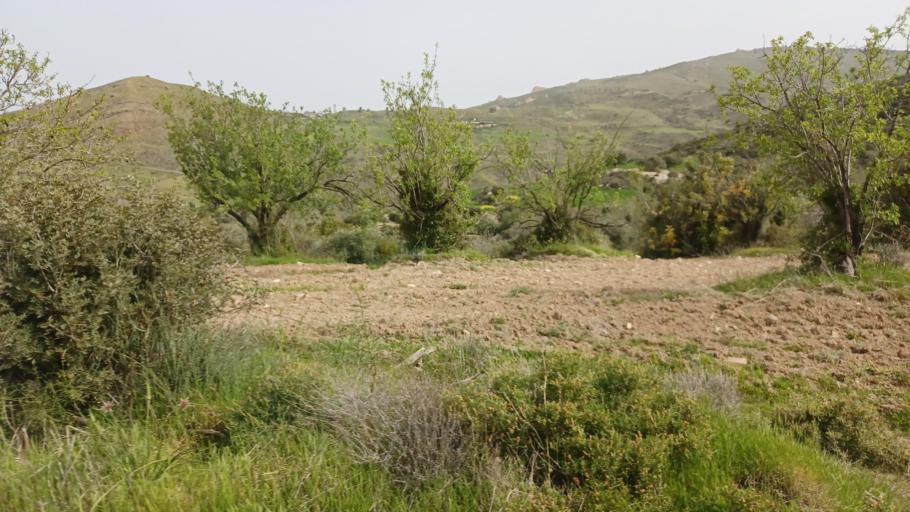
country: CY
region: Pafos
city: Pegeia
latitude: 34.9480
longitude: 32.3622
